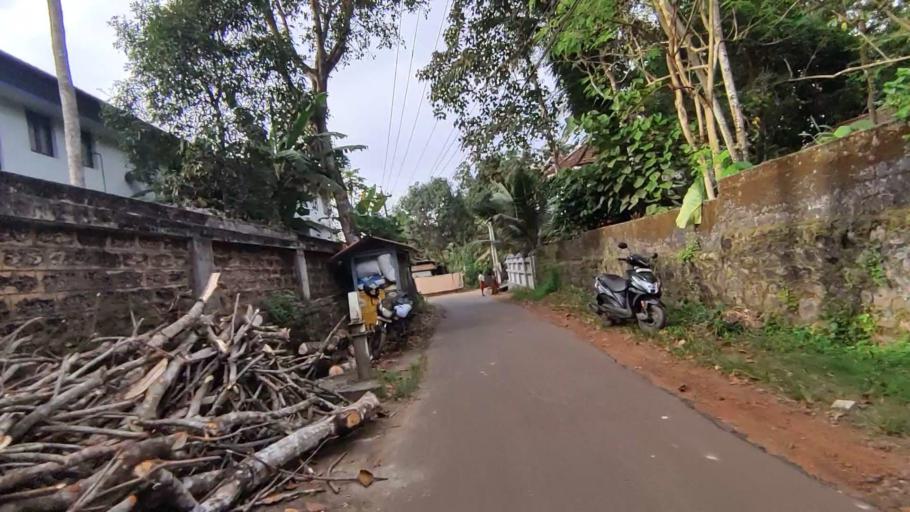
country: IN
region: Kerala
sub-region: Kottayam
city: Kottayam
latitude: 9.6105
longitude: 76.4849
